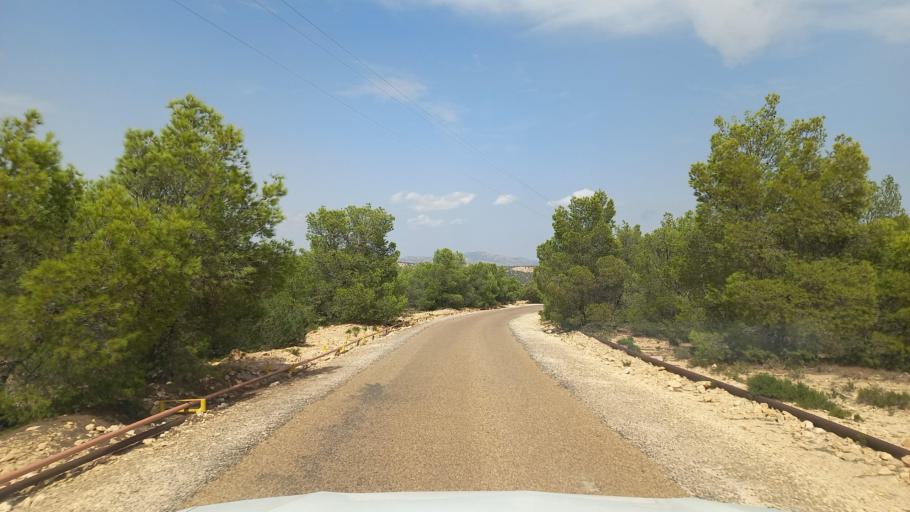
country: TN
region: Al Qasrayn
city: Sbiba
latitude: 35.3929
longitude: 8.9101
